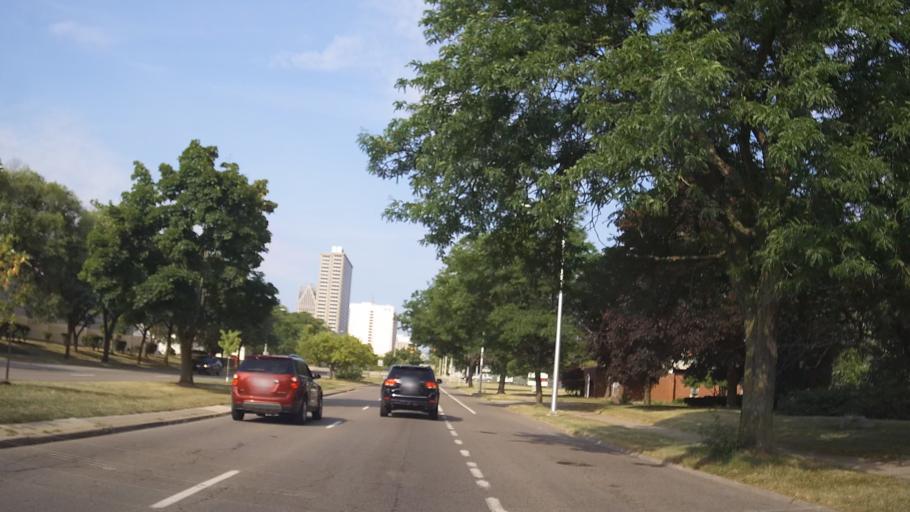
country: US
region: Michigan
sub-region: Wayne County
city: Detroit
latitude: 42.3400
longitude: -83.0280
